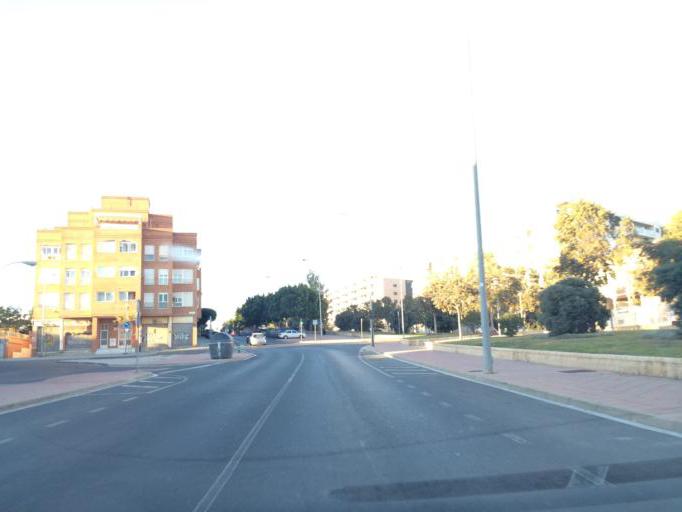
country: ES
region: Andalusia
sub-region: Provincia de Almeria
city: Almeria
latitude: 36.8528
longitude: -2.4394
